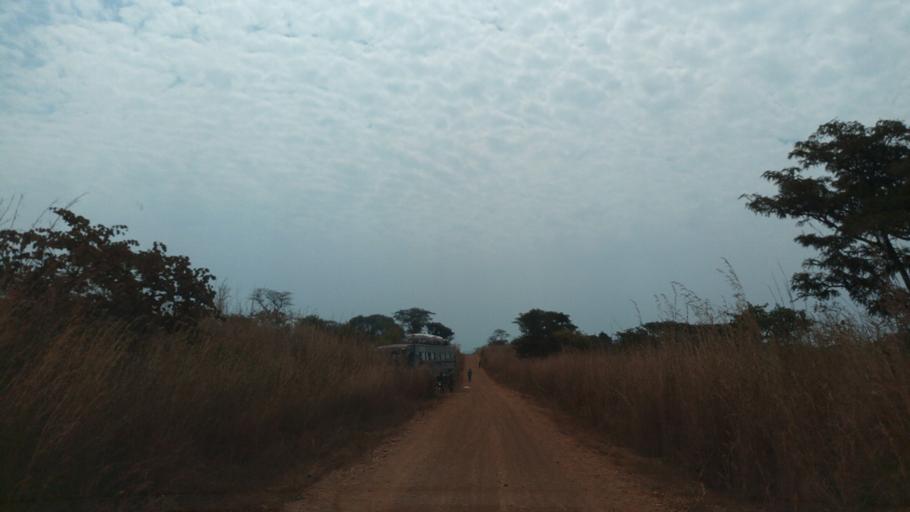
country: ZM
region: Northern
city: Kaputa
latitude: -8.2970
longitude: 29.0085
